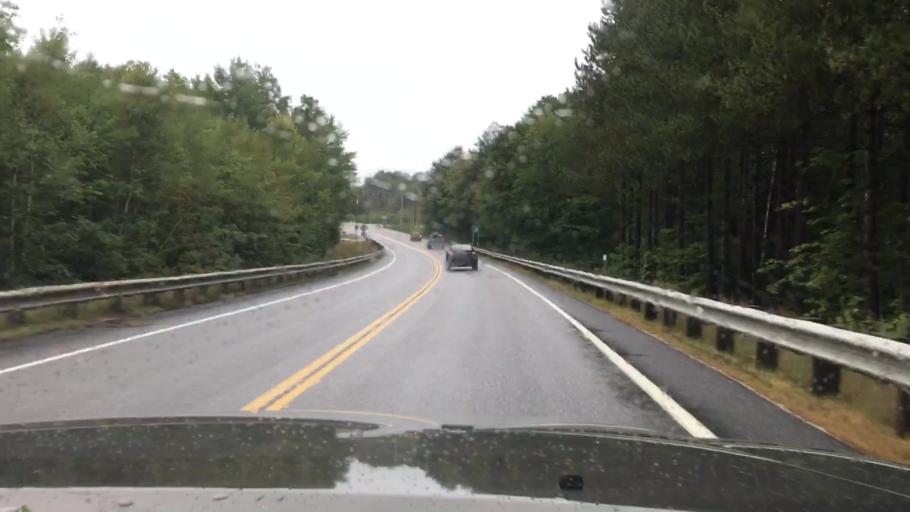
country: US
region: New Hampshire
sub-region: Cheshire County
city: Harrisville
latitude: 43.0593
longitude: -72.0759
